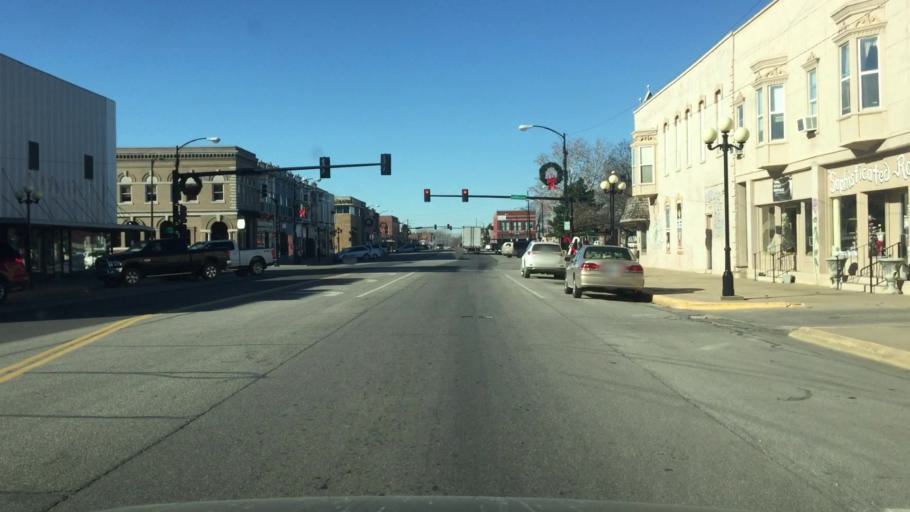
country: US
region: Kansas
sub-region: Allen County
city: Iola
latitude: 37.9214
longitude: -95.4027
